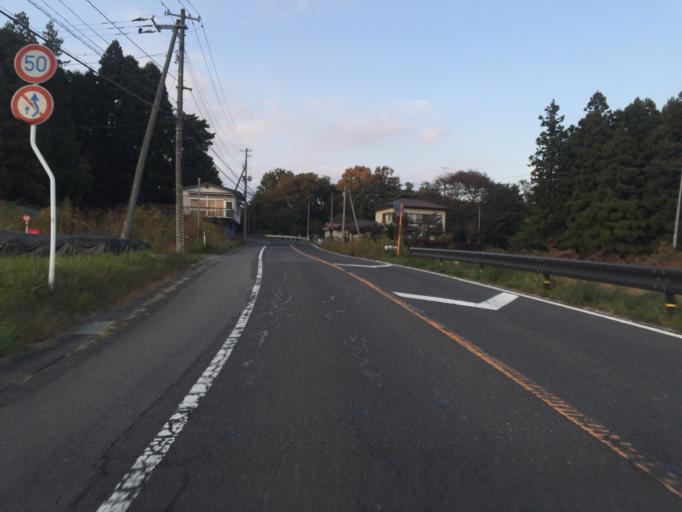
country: JP
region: Fukushima
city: Motomiya
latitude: 37.5692
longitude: 140.3512
